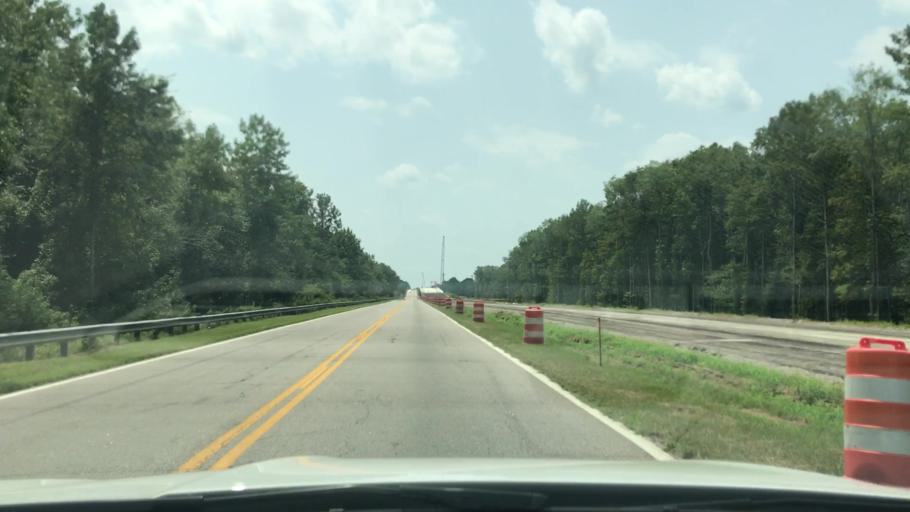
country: US
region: South Carolina
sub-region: Horry County
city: Socastee
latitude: 33.6656
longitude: -79.1472
